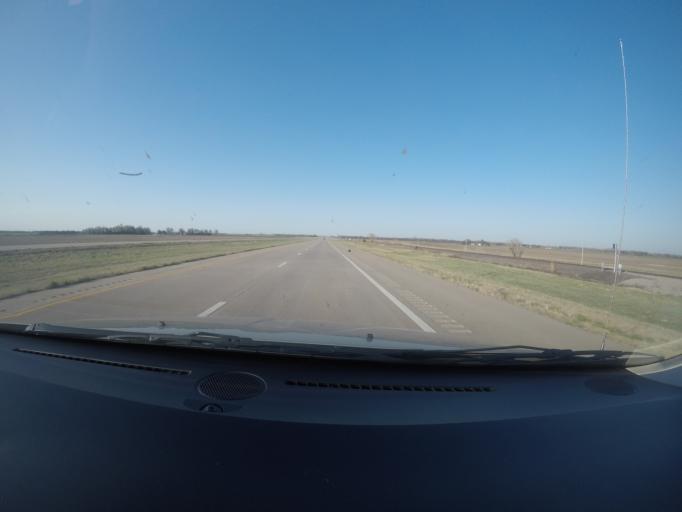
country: US
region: Kansas
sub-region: McPherson County
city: Inman
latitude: 38.2570
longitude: -97.7591
